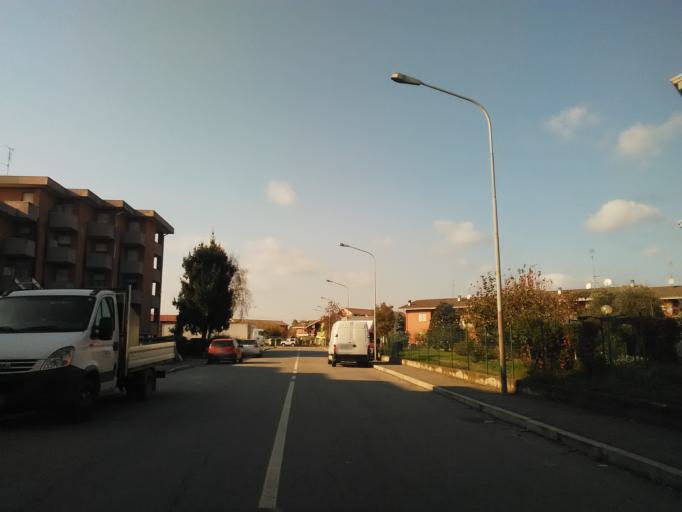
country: IT
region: Piedmont
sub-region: Provincia di Vercelli
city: Santhia
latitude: 45.3704
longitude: 8.1633
